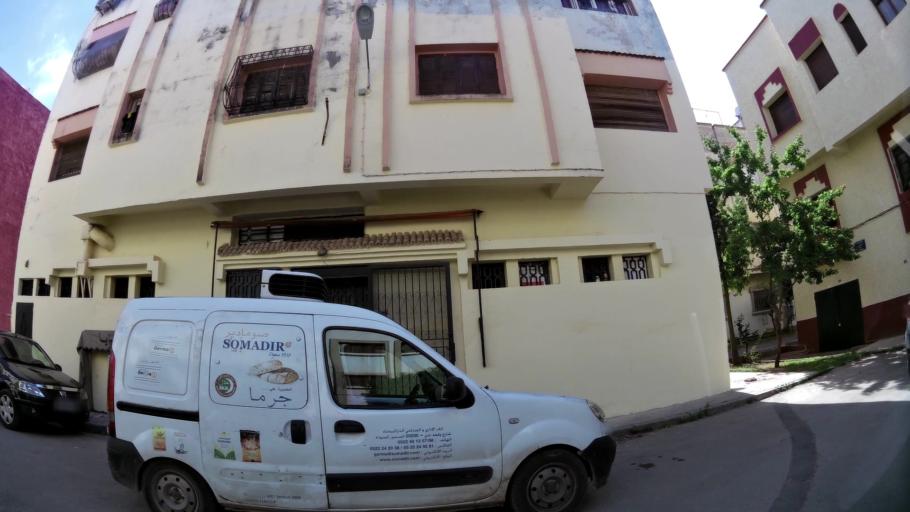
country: MA
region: Fes-Boulemane
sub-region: Fes
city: Fes
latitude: 34.0281
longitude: -5.0249
